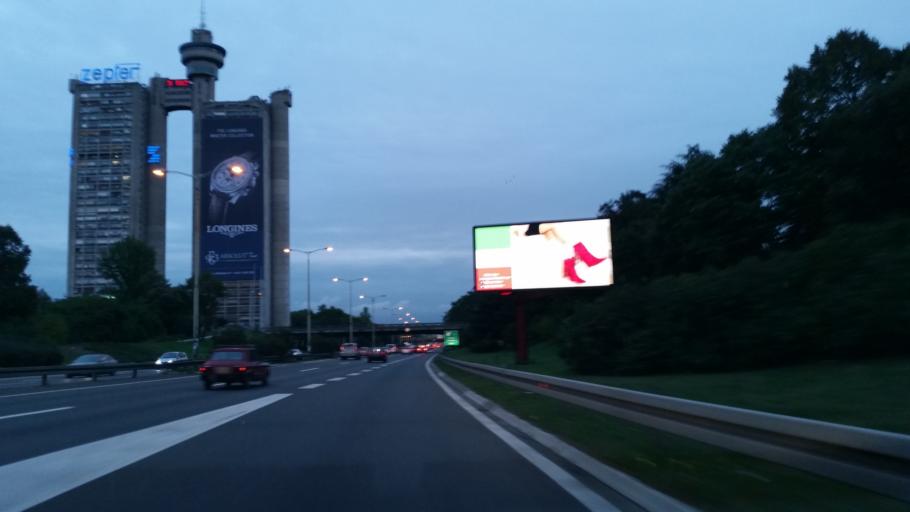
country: RS
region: Central Serbia
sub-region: Belgrade
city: Zemun
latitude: 44.8210
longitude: 20.4012
